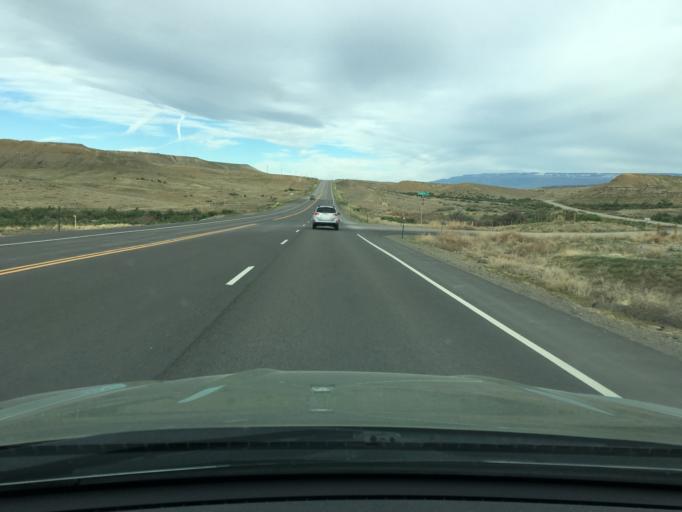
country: US
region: Colorado
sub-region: Delta County
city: Orchard City
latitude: 38.7975
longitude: -107.8386
